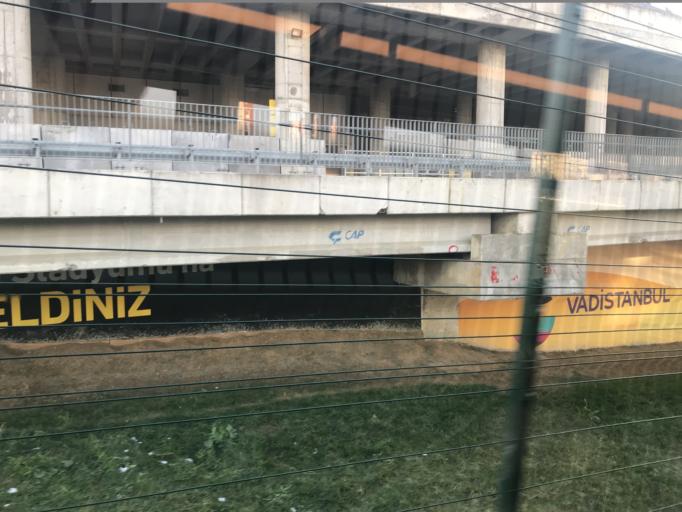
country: TR
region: Istanbul
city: Sisli
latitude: 41.1043
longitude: 28.9928
